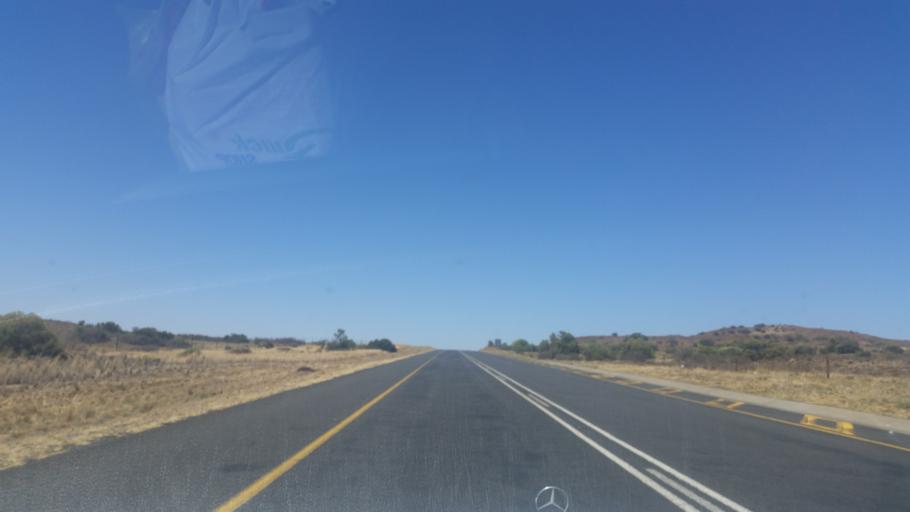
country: ZA
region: Northern Cape
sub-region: Pixley ka Seme District Municipality
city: Colesberg
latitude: -30.6187
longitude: 25.3214
